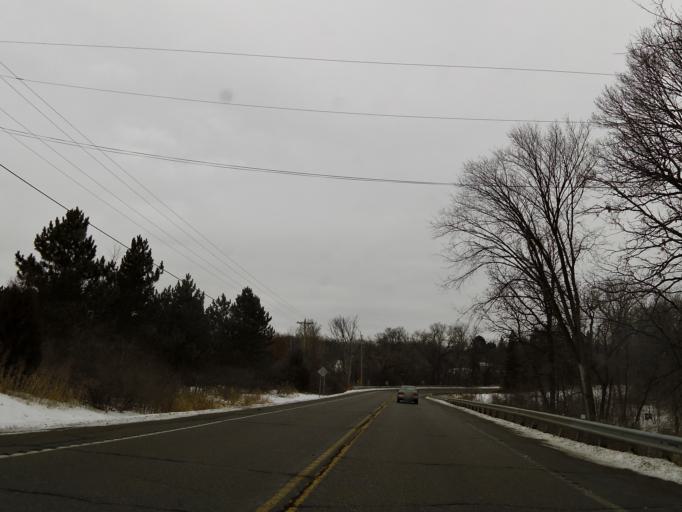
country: US
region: Minnesota
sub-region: Dakota County
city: Inver Grove Heights
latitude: 44.8154
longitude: -93.0853
